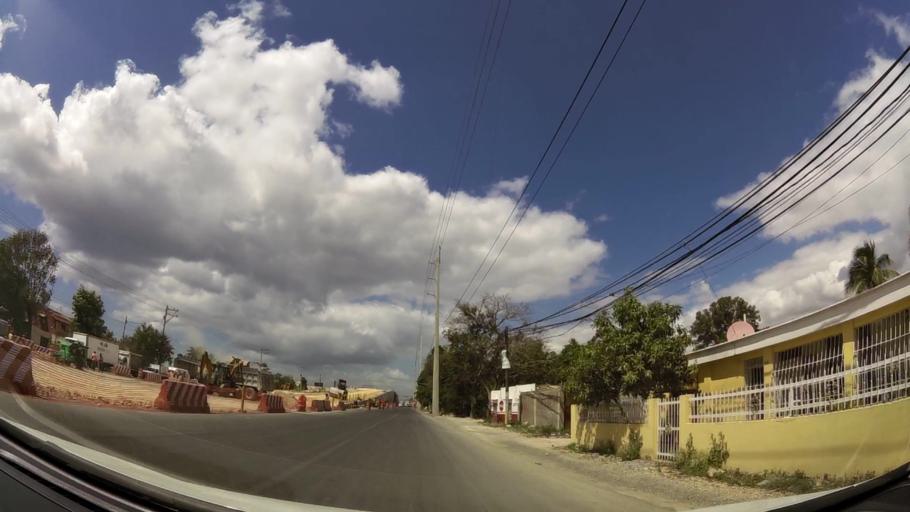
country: DO
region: Santo Domingo
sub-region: Santo Domingo
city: Boca Chica
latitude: 18.4487
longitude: -69.6506
